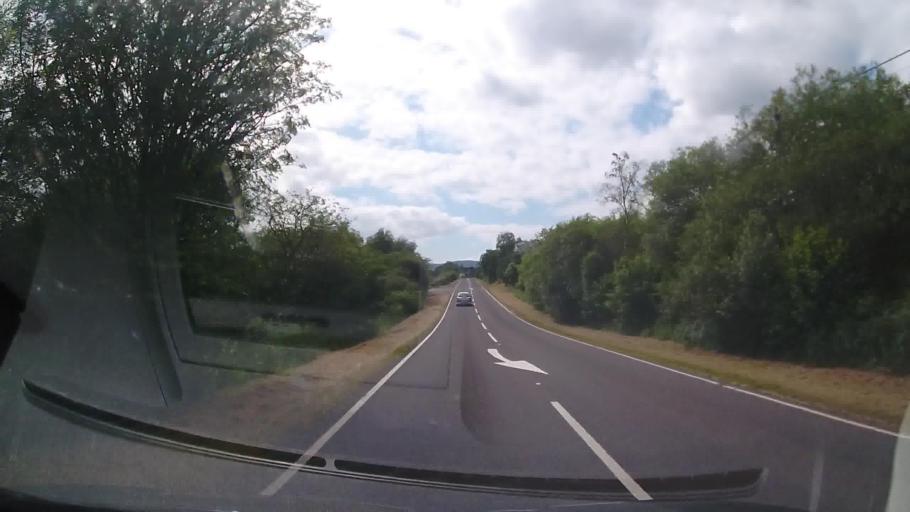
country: GB
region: Wales
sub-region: Gwynedd
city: Trawsfynydd
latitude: 52.9065
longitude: -3.8955
